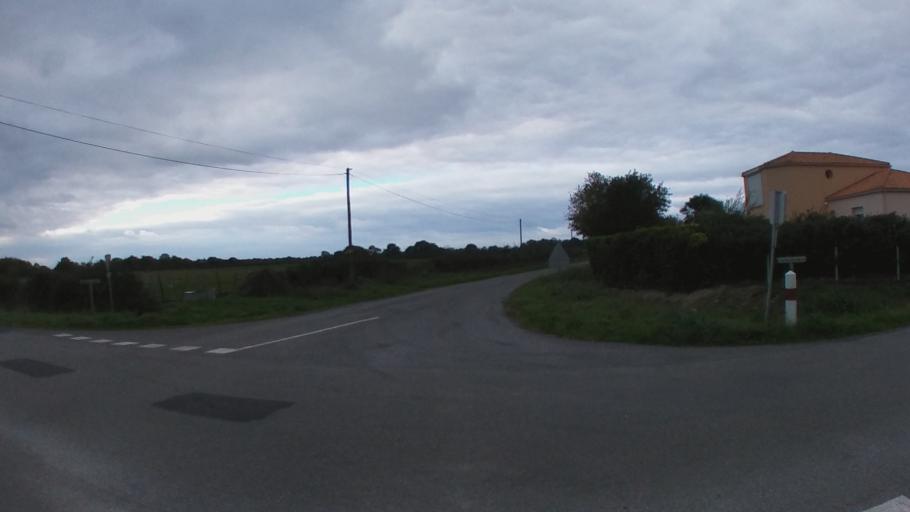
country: FR
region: Pays de la Loire
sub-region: Departement de la Loire-Atlantique
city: Corsept
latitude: 47.2716
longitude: -2.0761
